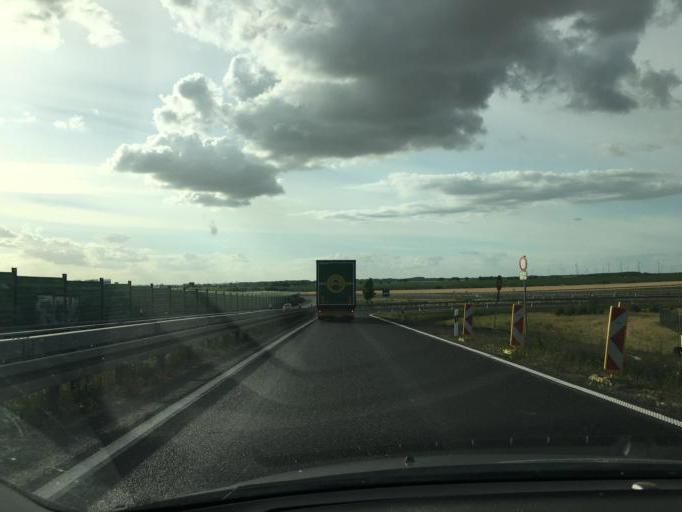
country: DE
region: Saxony-Anhalt
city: Ilberstedt
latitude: 51.8039
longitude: 11.6821
